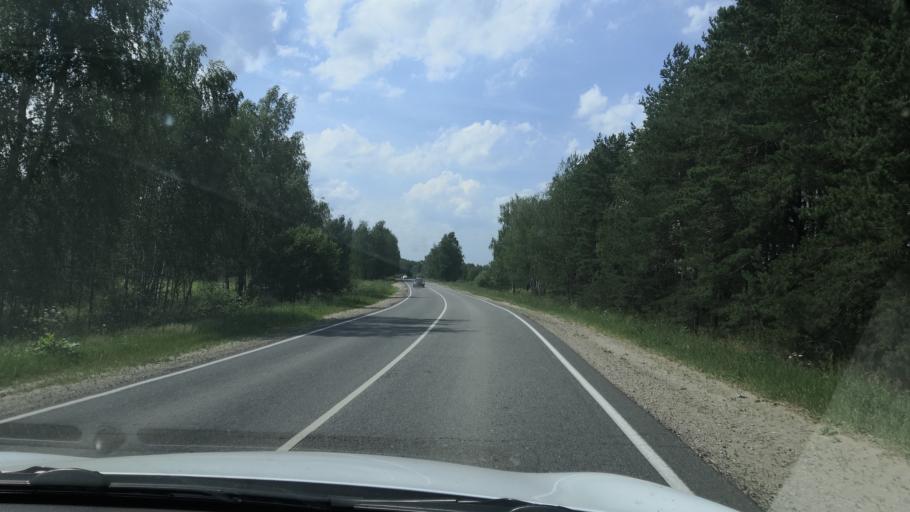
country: RU
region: Rjazan
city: Murmino
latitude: 54.5918
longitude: 40.1018
